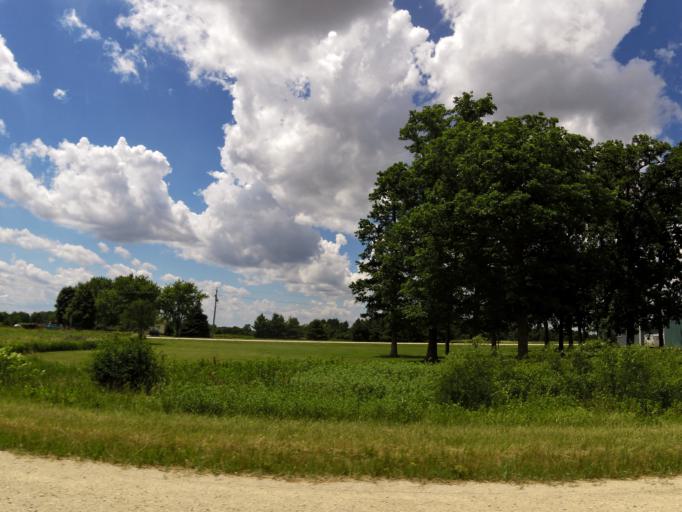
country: US
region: Iowa
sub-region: Fayette County
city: Oelwein
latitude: 42.5885
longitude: -91.9037
